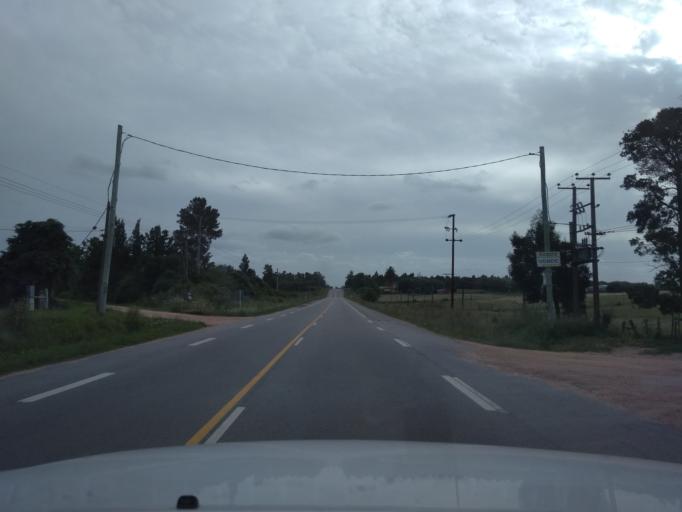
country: UY
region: Canelones
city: Joaquin Suarez
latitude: -34.6876
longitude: -56.0247
